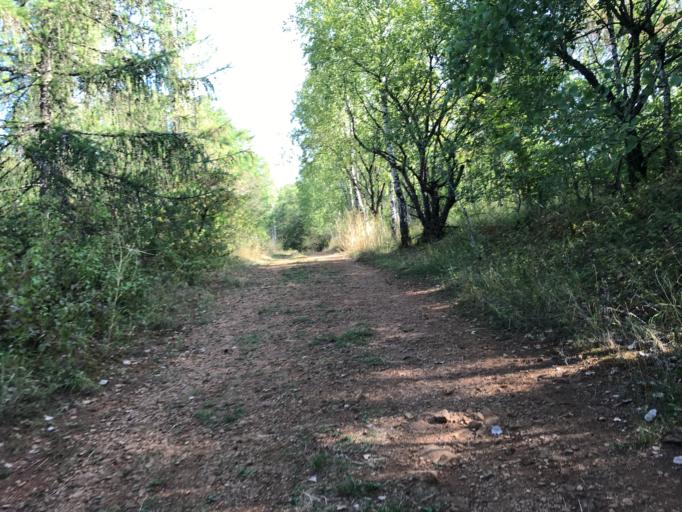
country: LU
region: Luxembourg
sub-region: Canton d'Esch-sur-Alzette
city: Petange
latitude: 49.5428
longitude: 5.8760
